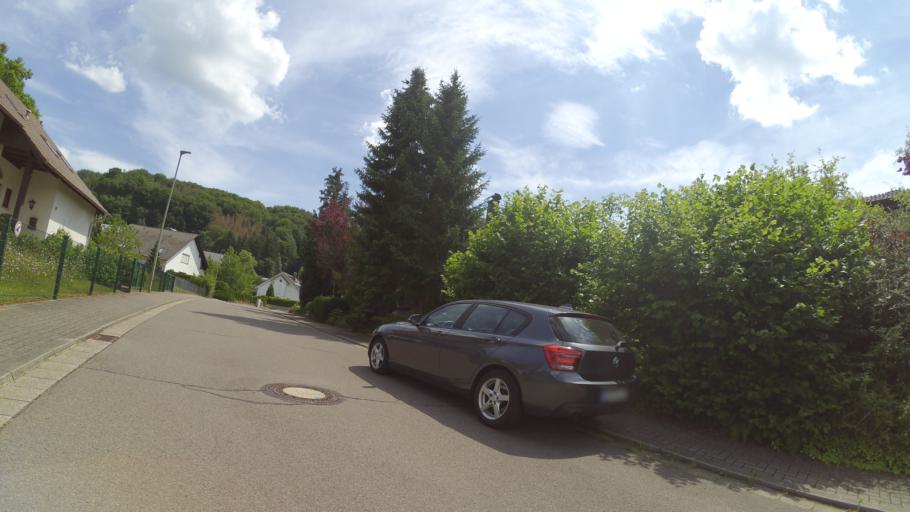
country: DE
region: Rheinland-Pfalz
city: Grossbundenbach
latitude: 49.3095
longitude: 7.3791
